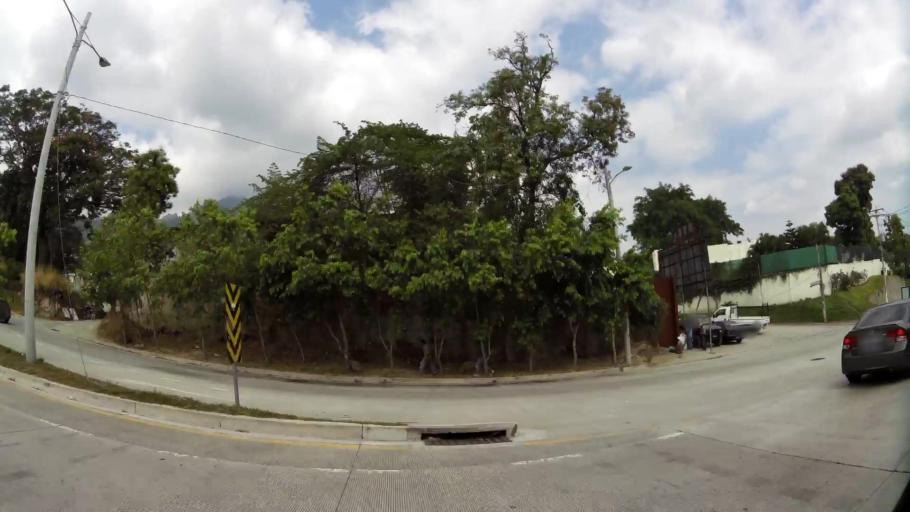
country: SV
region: San Salvador
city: Mejicanos
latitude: 13.7142
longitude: -89.2420
